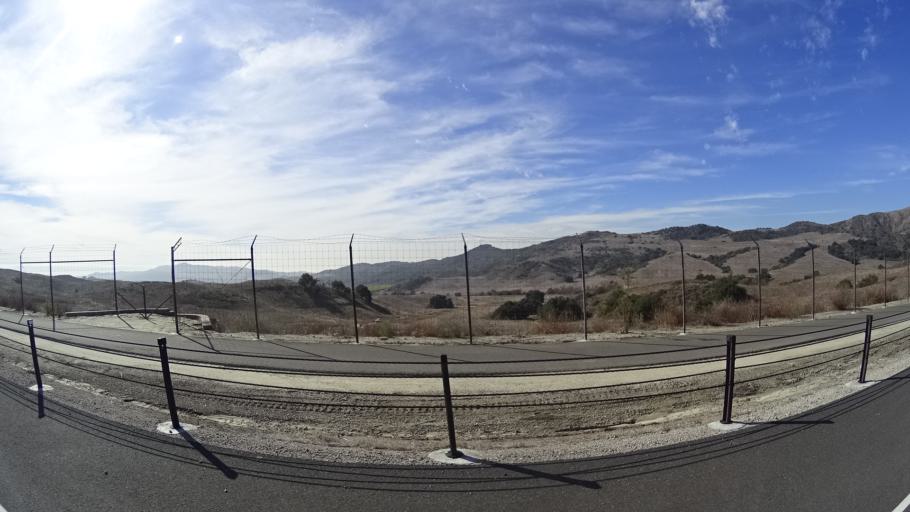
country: US
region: California
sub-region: Orange County
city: Ladera Ranch
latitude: 33.5612
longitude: -117.6054
